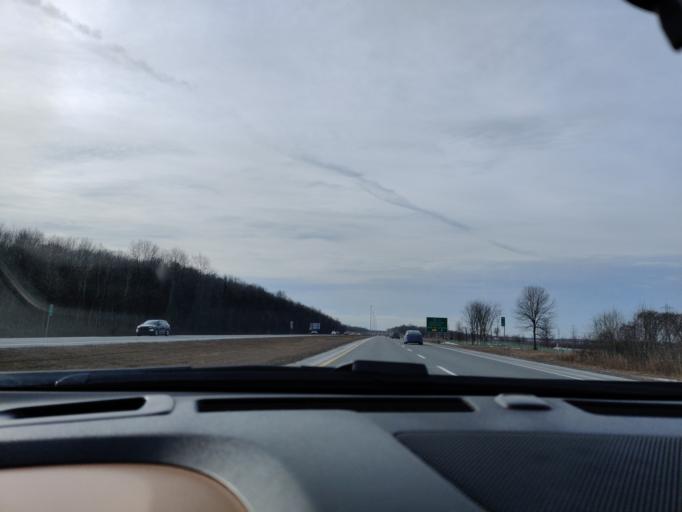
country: CA
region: Quebec
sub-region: Monteregie
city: Les Coteaux
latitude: 45.2884
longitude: -74.1960
